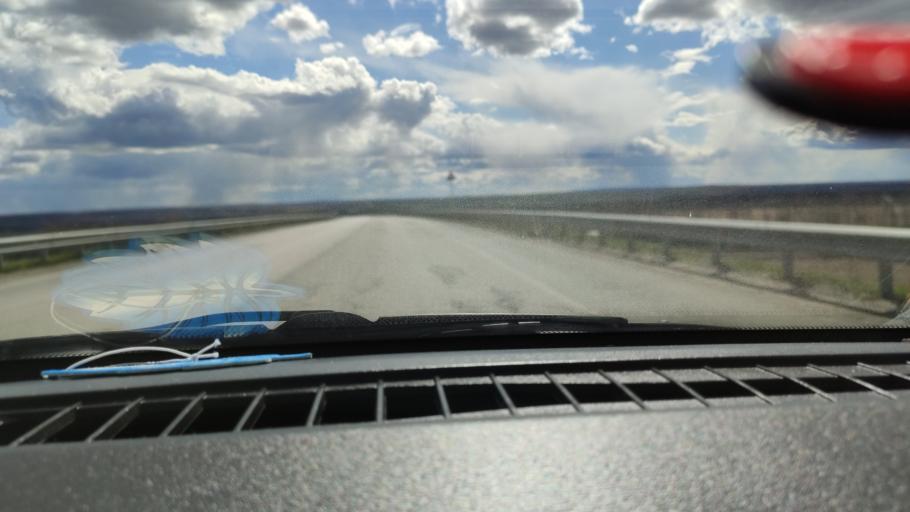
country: RU
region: Samara
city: Varlamovo
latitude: 53.1705
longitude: 48.2810
